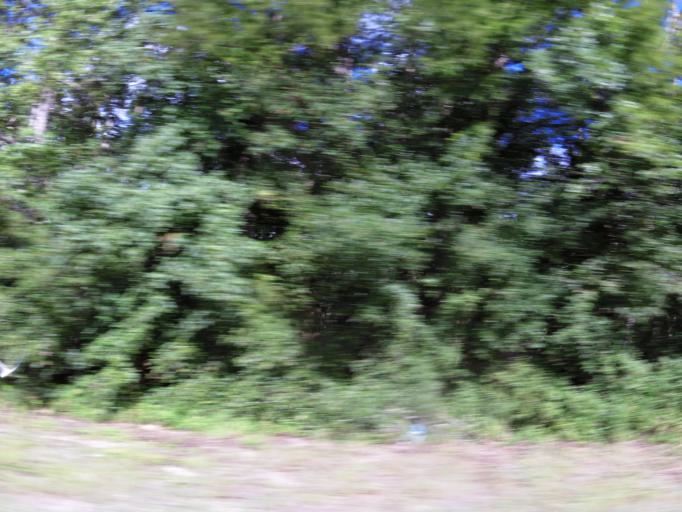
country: US
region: Georgia
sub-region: Camden County
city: Kingsland
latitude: 30.8639
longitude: -81.7030
